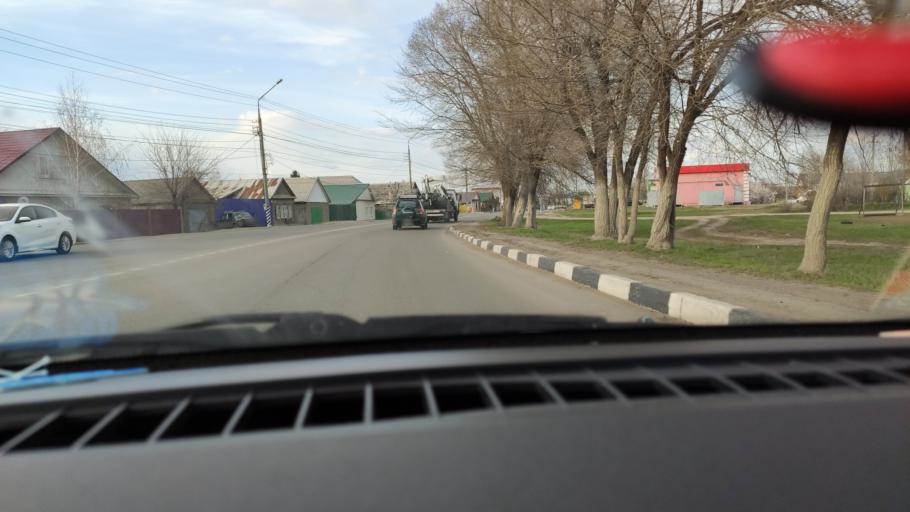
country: RU
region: Saratov
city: Privolzhskiy
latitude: 51.4269
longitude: 46.0490
